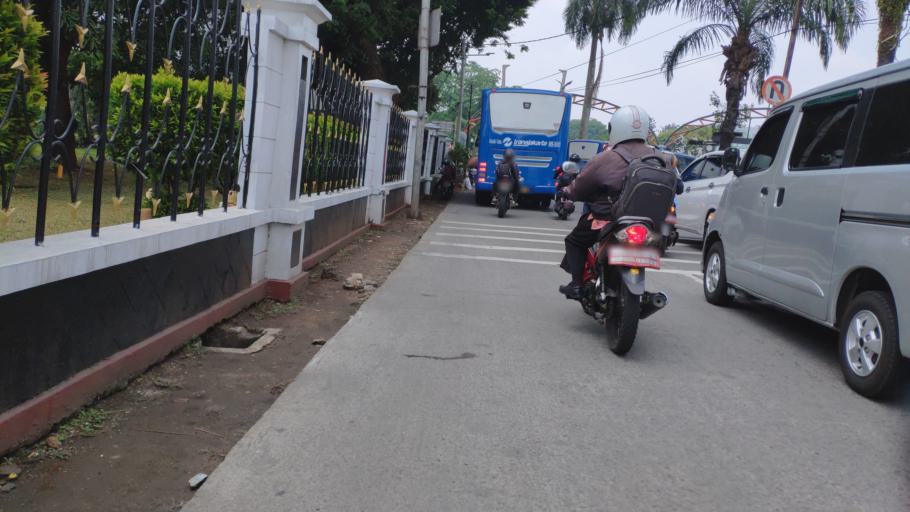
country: ID
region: West Java
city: Pamulang
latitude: -6.3054
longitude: 106.8207
